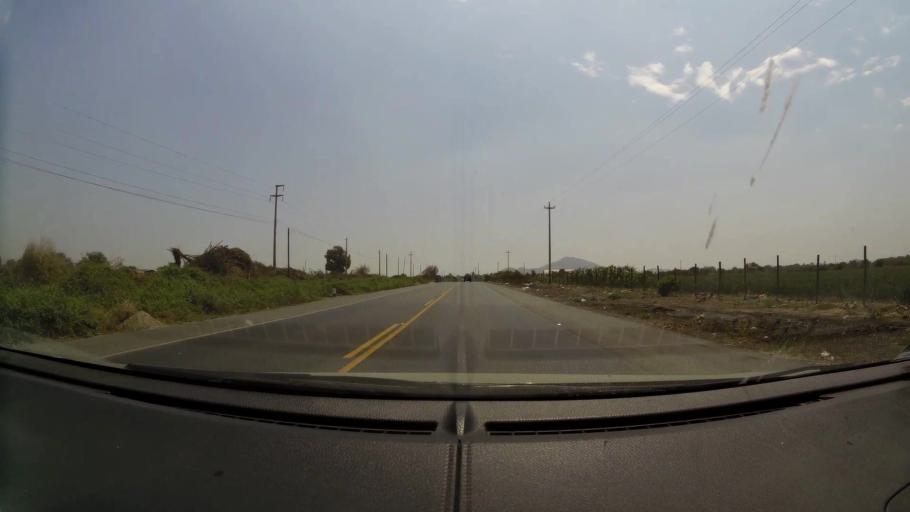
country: PE
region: La Libertad
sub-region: Chepen
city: Pacanga
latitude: -7.1352
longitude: -79.4688
